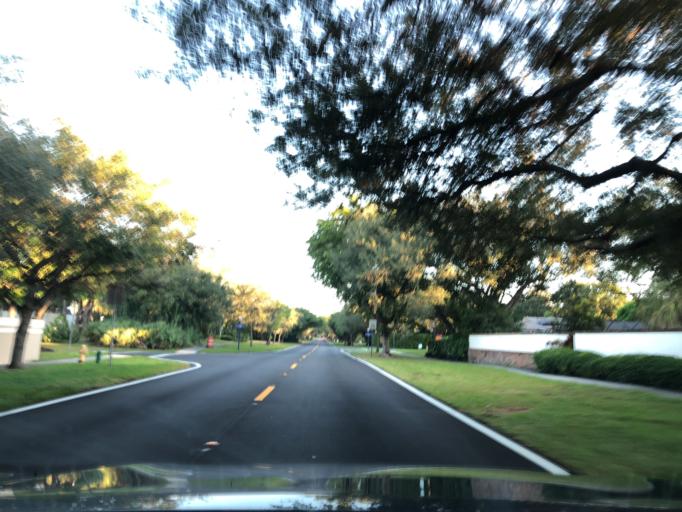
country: US
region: Florida
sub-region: Miami-Dade County
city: Palmetto Bay
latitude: 25.6250
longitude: -80.3251
